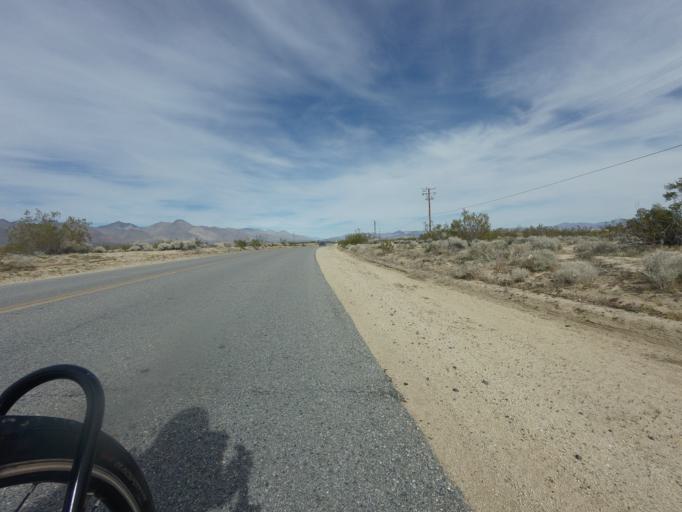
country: US
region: California
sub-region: Kern County
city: Inyokern
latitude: 35.7083
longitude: -117.8309
